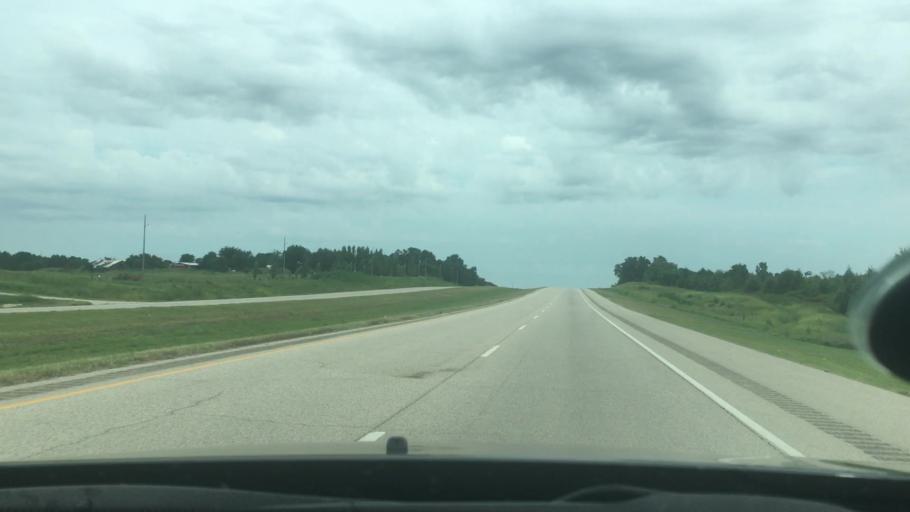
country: US
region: Oklahoma
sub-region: Pontotoc County
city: Byng
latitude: 34.9136
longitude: -96.6798
